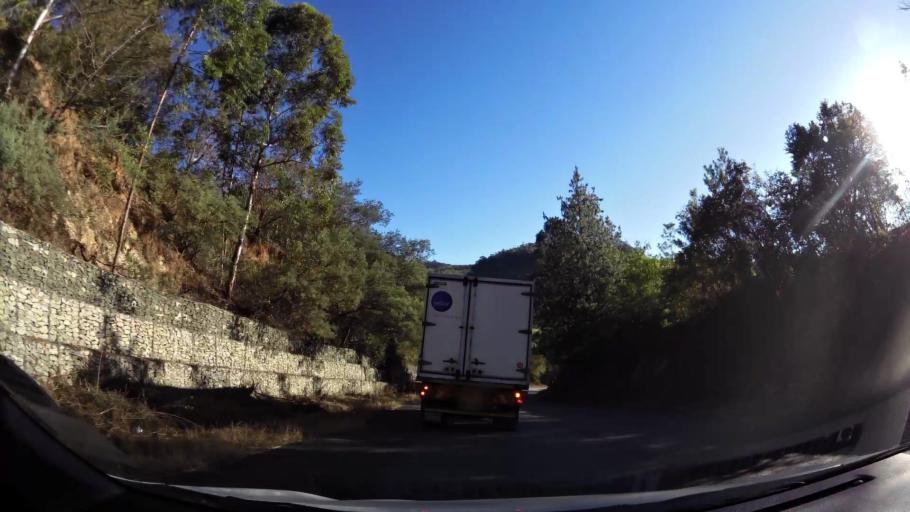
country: ZA
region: Limpopo
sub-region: Mopani District Municipality
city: Tzaneen
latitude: -23.9345
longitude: 30.0273
